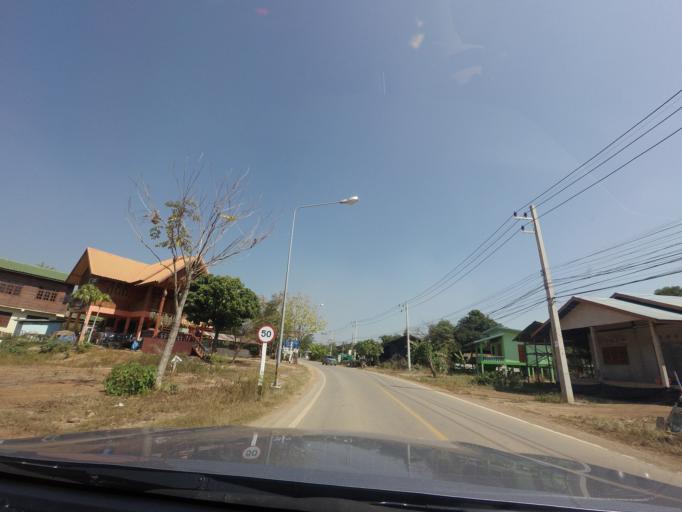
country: TH
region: Sukhothai
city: Si Samrong
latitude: 17.2221
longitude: 99.7743
